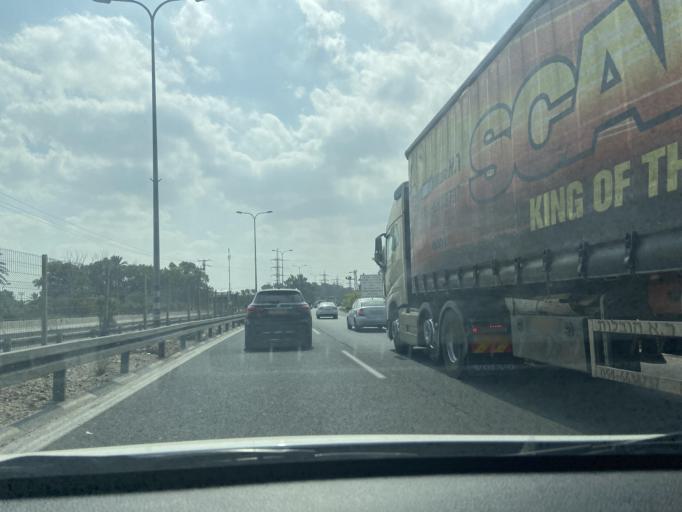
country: IL
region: Northern District
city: `Akko
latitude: 32.8987
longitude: 35.0926
